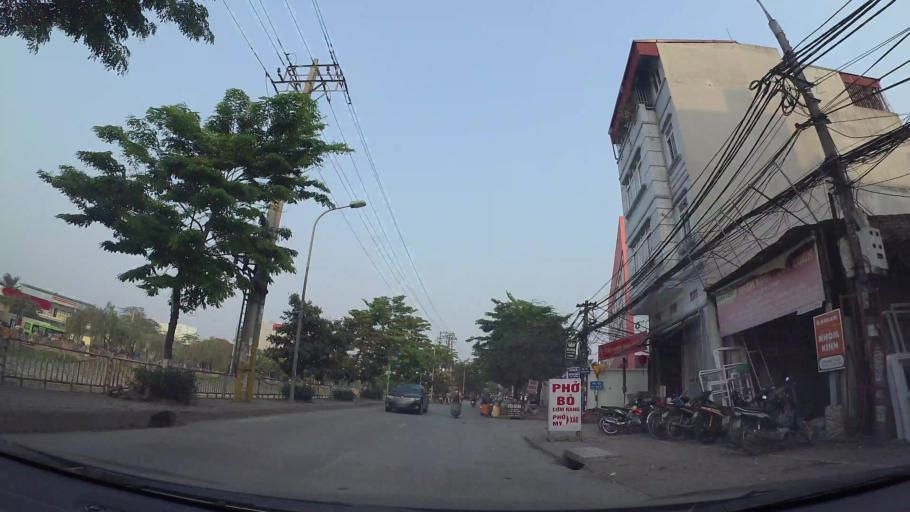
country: VN
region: Ha Noi
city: Thanh Xuan
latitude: 20.9789
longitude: 105.8215
